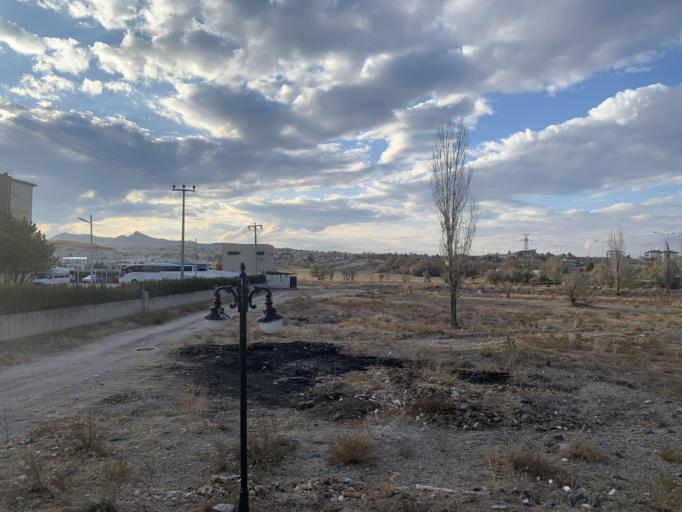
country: TR
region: Nevsehir
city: Avanos
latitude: 38.7034
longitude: 34.8388
